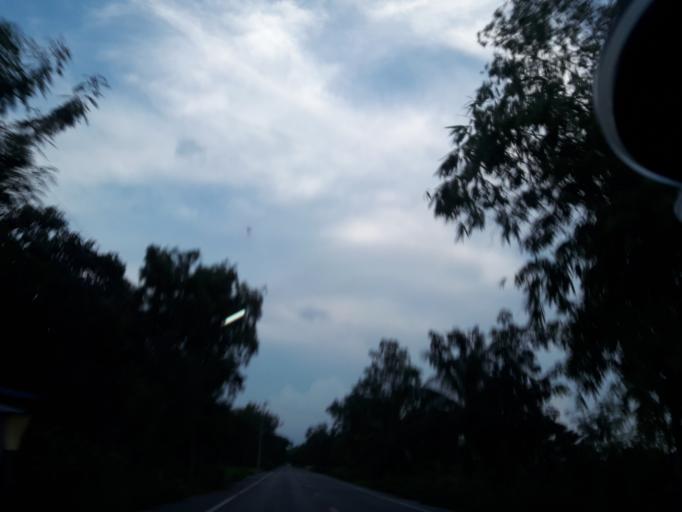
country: TH
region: Pathum Thani
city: Nong Suea
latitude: 14.1577
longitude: 100.8690
